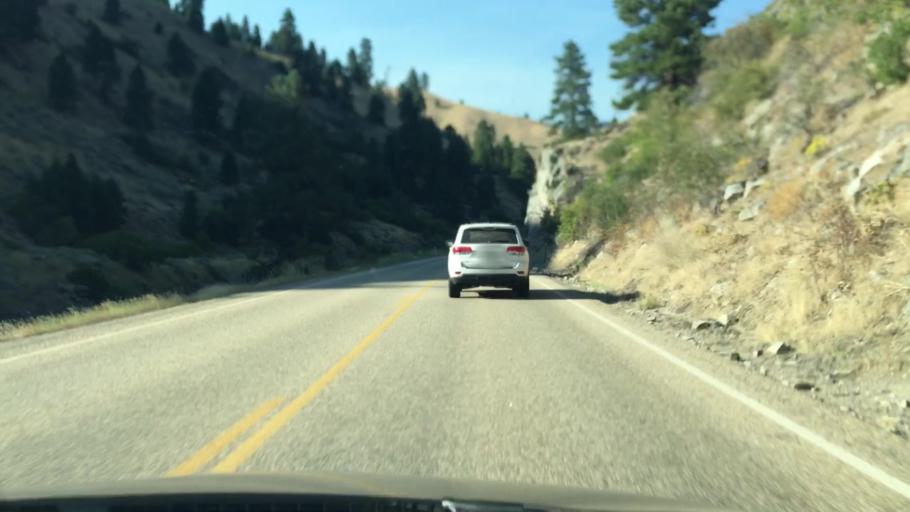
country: US
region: Idaho
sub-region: Boise County
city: Idaho City
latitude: 44.0930
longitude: -116.1023
